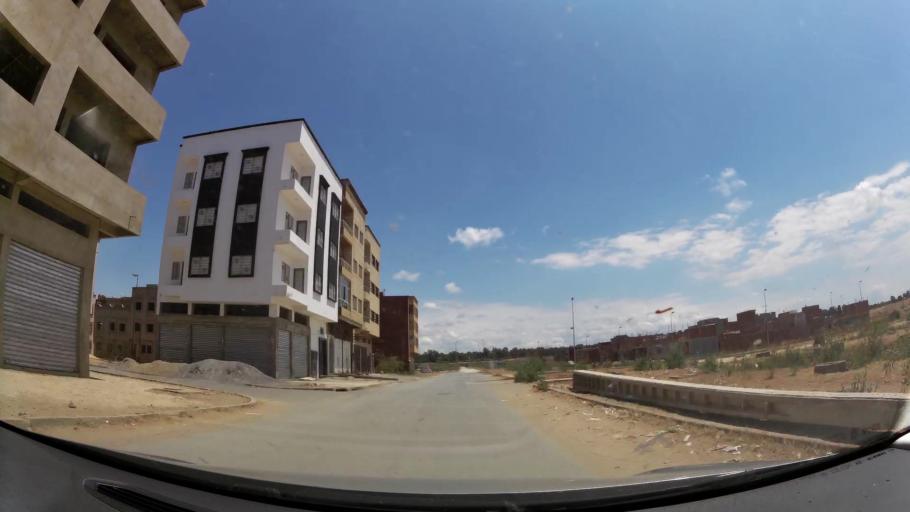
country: MA
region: Gharb-Chrarda-Beni Hssen
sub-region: Kenitra Province
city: Kenitra
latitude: 34.2309
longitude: -6.6117
